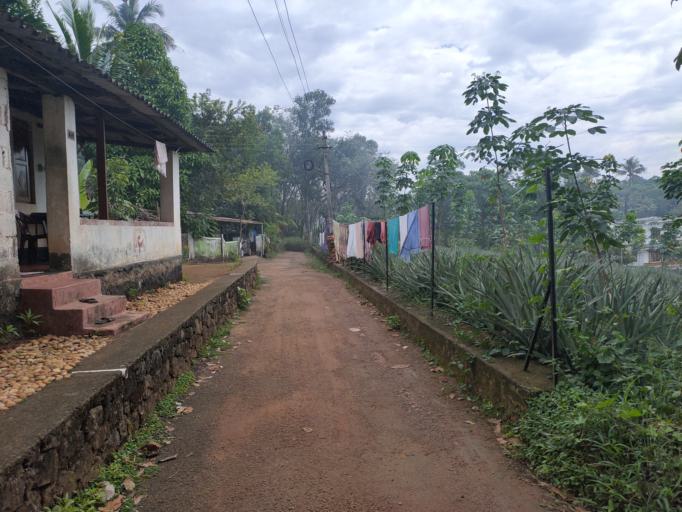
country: IN
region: Kerala
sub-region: Ernakulam
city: Kotamangalam
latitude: 9.9988
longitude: 76.6410
